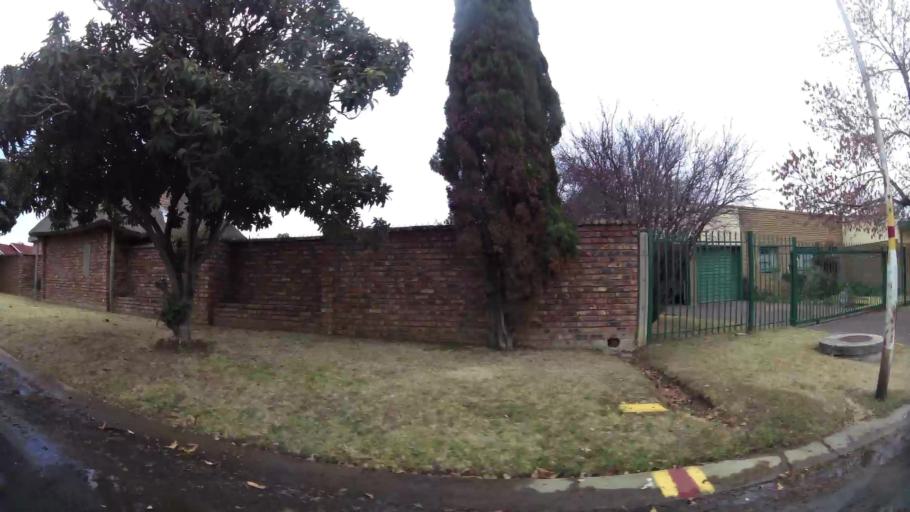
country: ZA
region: Orange Free State
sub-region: Fezile Dabi District Municipality
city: Kroonstad
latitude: -27.6336
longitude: 27.2448
